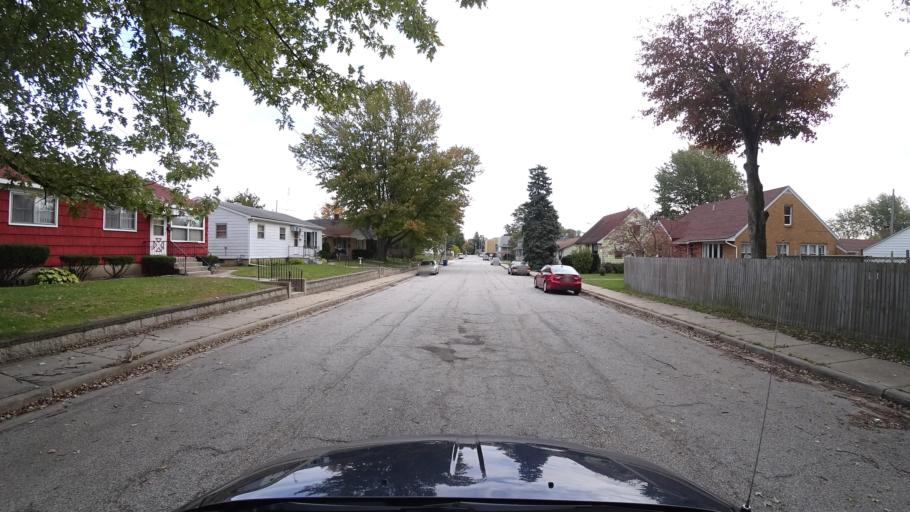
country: US
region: Indiana
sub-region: LaPorte County
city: Michigan City
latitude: 41.7041
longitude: -86.8984
